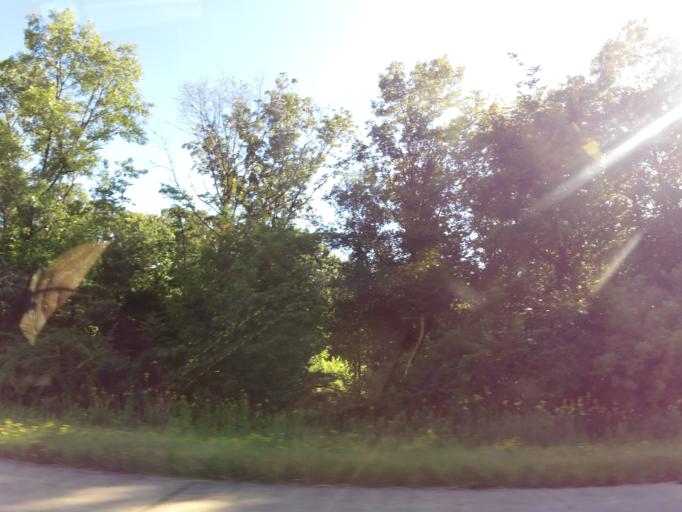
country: US
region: Missouri
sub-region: Pike County
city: Bowling Green
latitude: 39.3884
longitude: -91.2305
